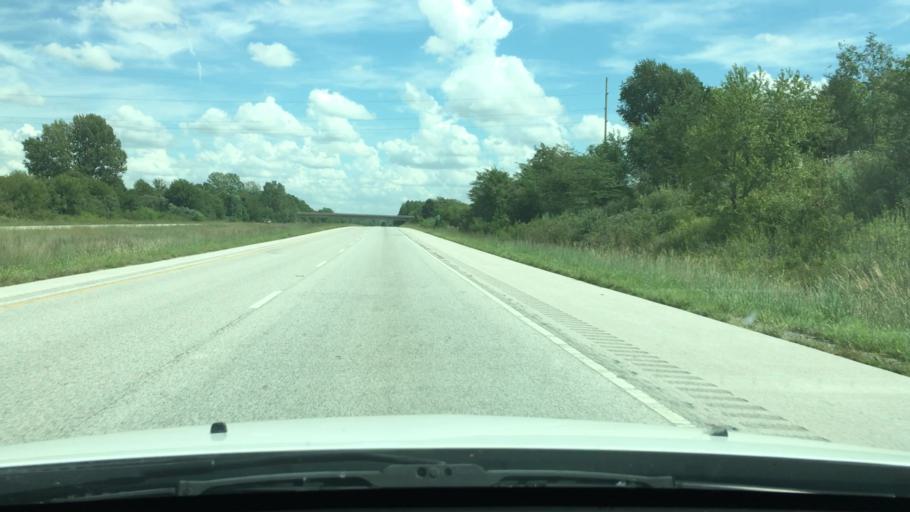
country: US
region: Illinois
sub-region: Scott County
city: Winchester
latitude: 39.6812
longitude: -90.4206
